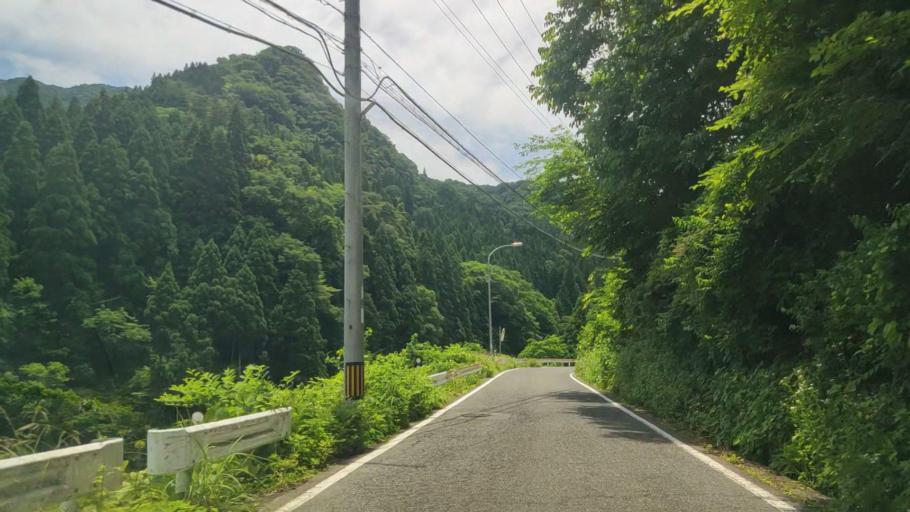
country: JP
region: Tottori
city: Tottori
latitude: 35.4369
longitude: 134.5325
